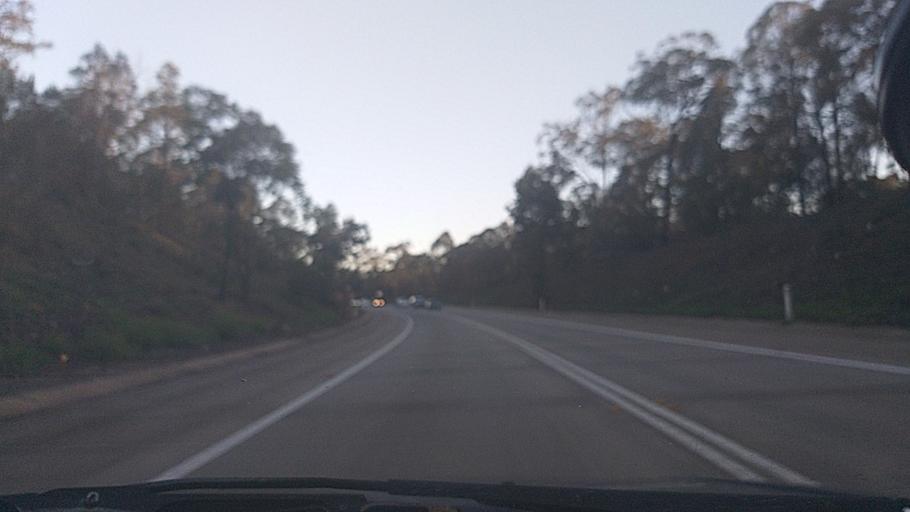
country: AU
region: New South Wales
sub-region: Wollondilly
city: Douglas Park
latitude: -34.2558
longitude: 150.7052
